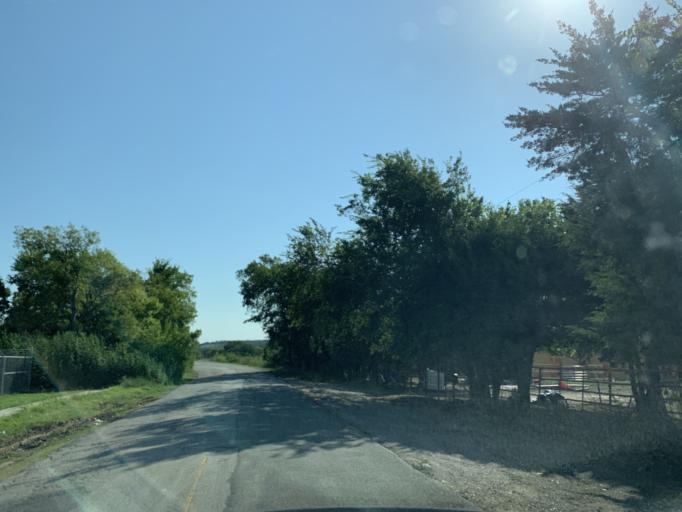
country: US
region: Texas
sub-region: Dallas County
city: Hutchins
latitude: 32.6575
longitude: -96.7488
